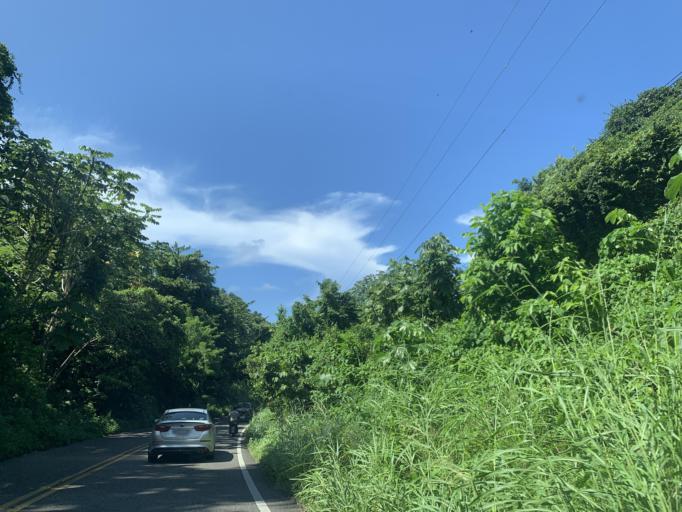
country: DO
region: Maria Trinidad Sanchez
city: Cabrera
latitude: 19.6579
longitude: -69.9378
